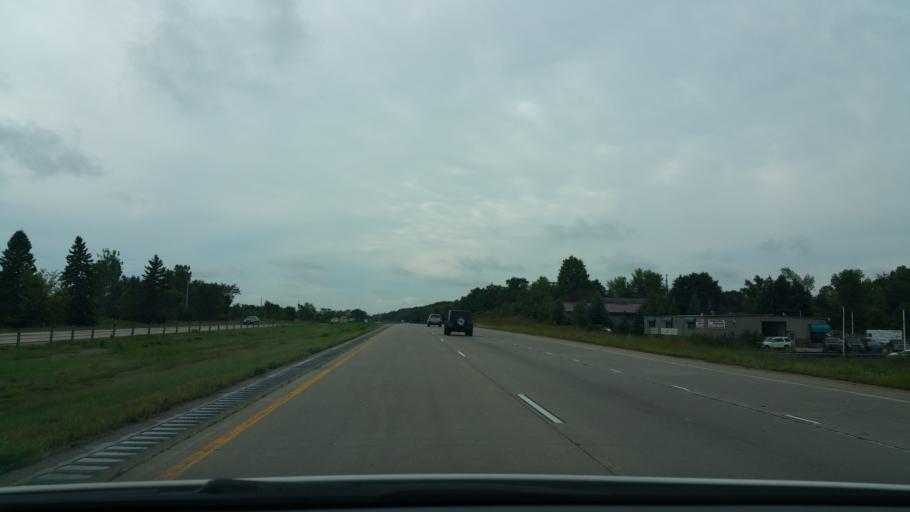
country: US
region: Minnesota
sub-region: Dakota County
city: Lakeville
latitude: 44.6399
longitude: -93.2972
